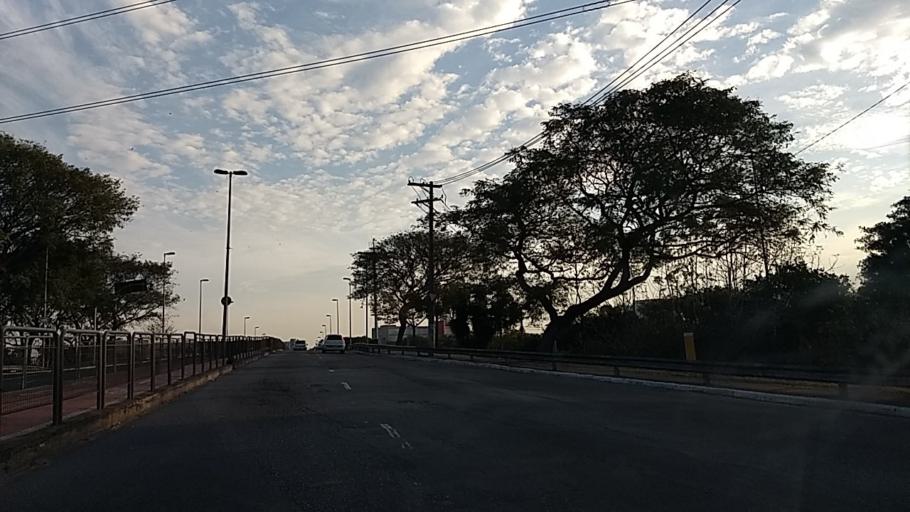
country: BR
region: Sao Paulo
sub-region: Sao Paulo
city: Sao Paulo
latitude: -23.5258
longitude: -46.5956
